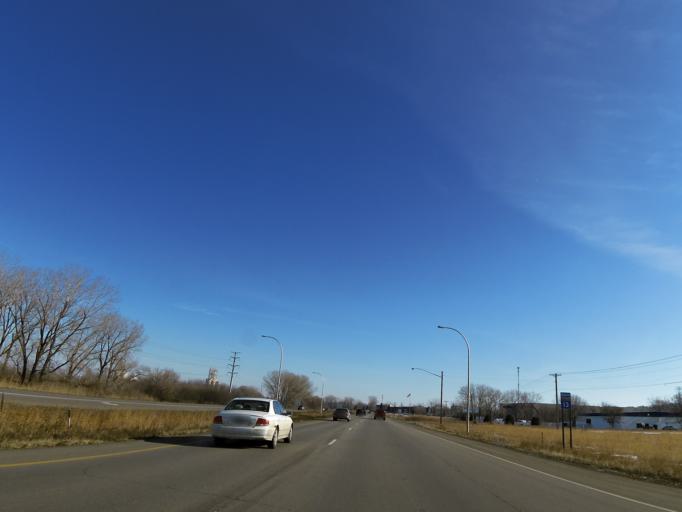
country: US
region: Minnesota
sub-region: Scott County
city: Savage
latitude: 44.7779
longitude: -93.3704
